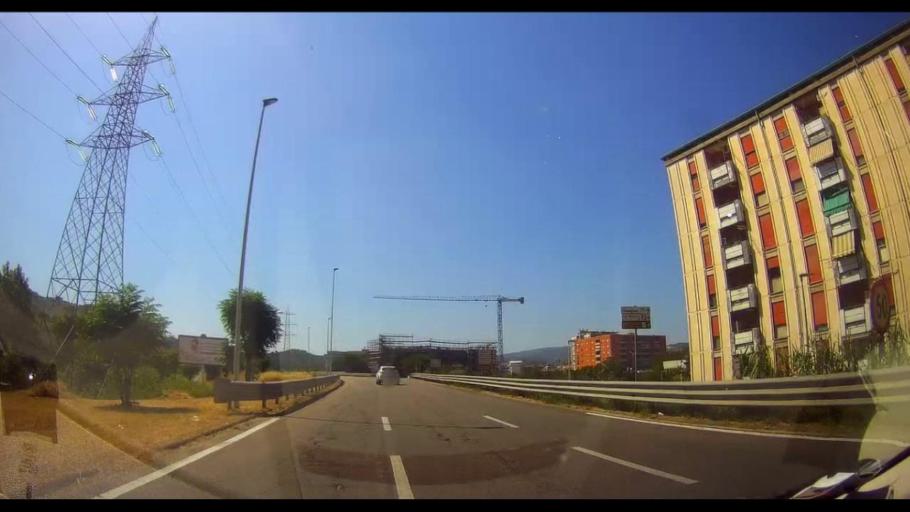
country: IT
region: Calabria
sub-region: Provincia di Cosenza
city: Cosenza
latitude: 39.3147
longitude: 16.2587
